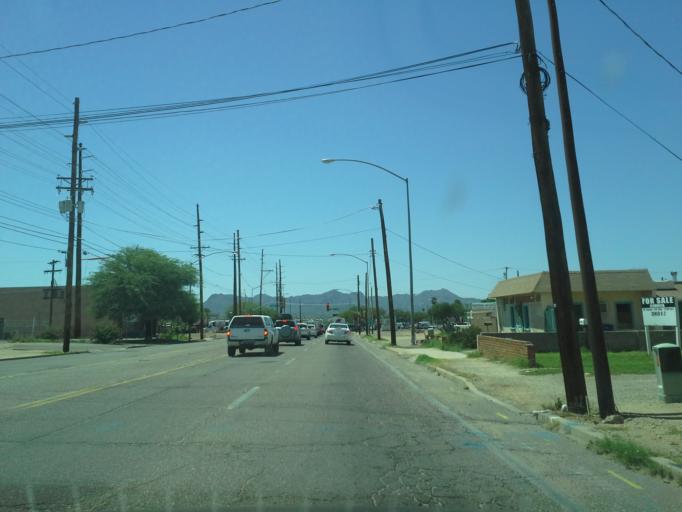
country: US
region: Arizona
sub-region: Pima County
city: South Tucson
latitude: 32.2504
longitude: -110.9703
